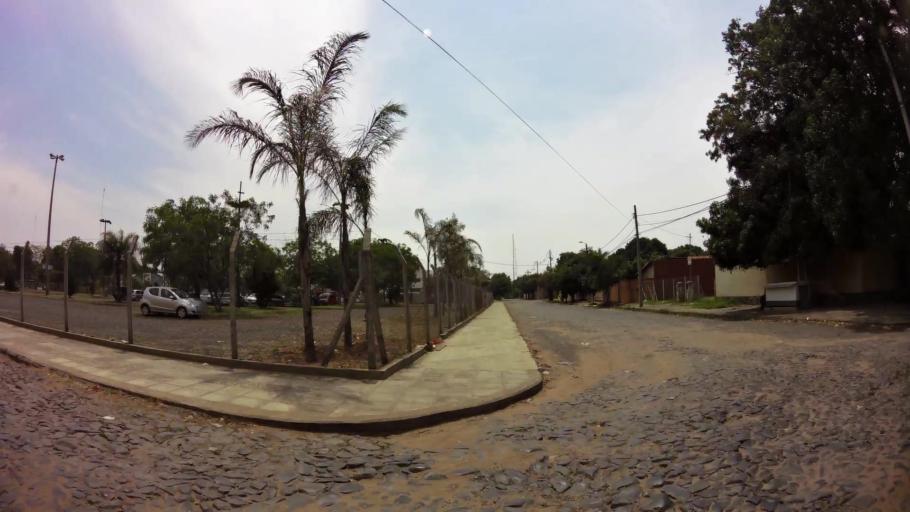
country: PY
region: Central
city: Lambare
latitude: -25.3157
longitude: -57.5692
